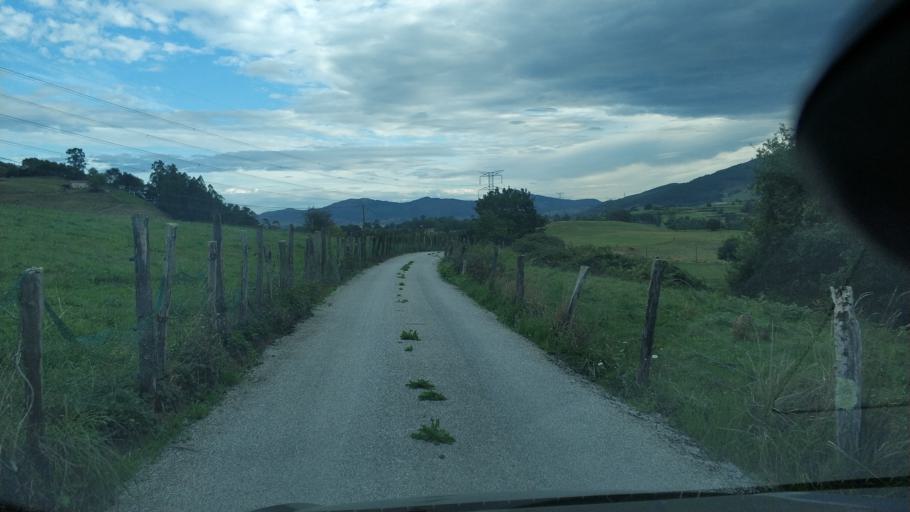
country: ES
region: Cantabria
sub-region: Provincia de Cantabria
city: Santa Maria de Cayon
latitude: 43.2915
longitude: -3.8573
